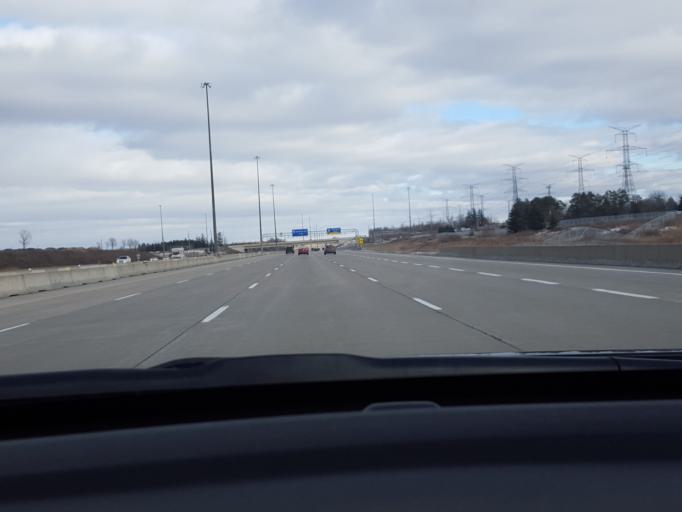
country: CA
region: Ontario
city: Markham
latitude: 43.8540
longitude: -79.2908
